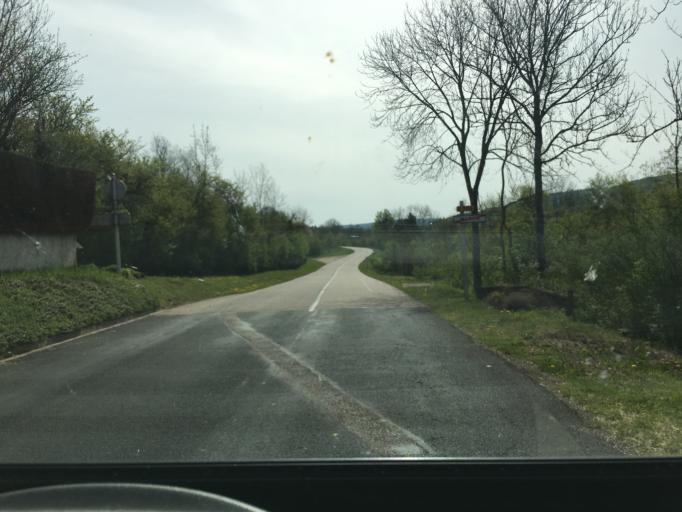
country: FR
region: Lorraine
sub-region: Departement de Meurthe-et-Moselle
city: Chaligny
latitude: 48.6285
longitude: 6.0544
